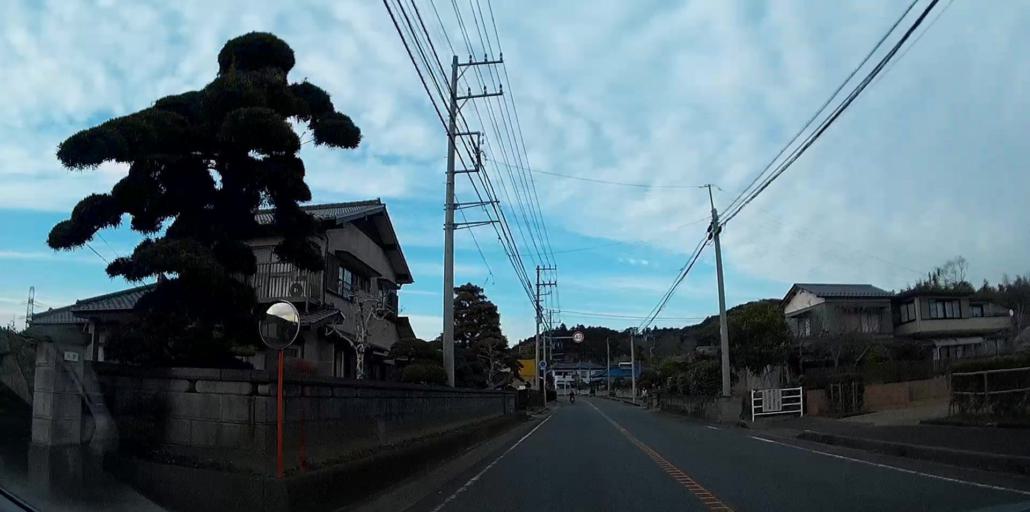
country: JP
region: Chiba
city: Kisarazu
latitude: 35.3753
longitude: 140.0621
